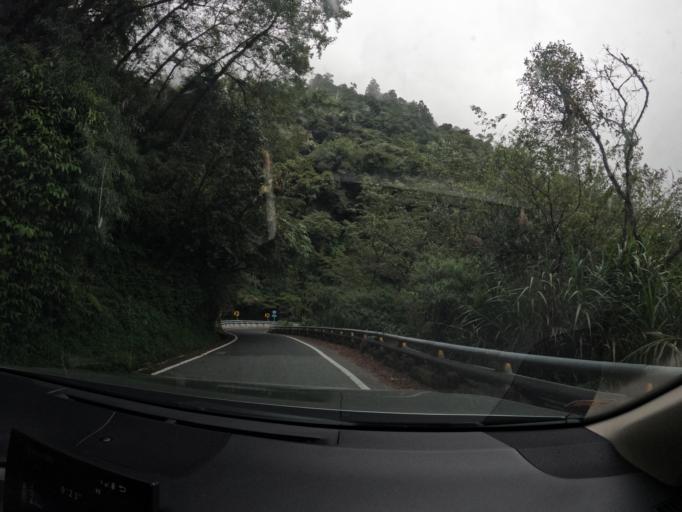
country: TW
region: Taiwan
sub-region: Taitung
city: Taitung
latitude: 23.2447
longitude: 120.9965
